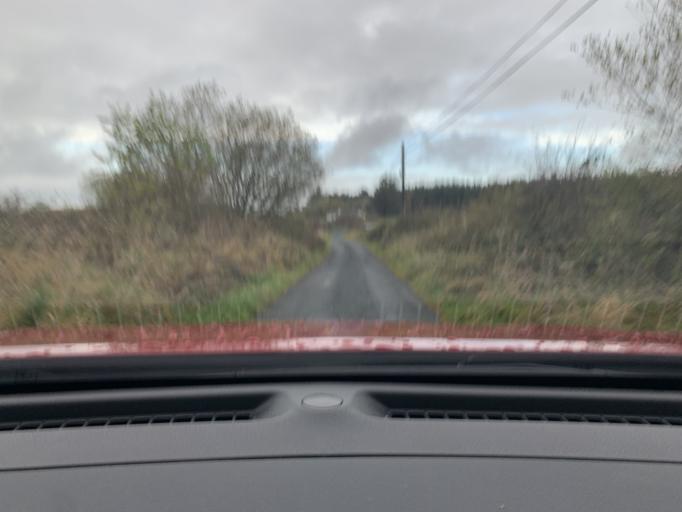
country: IE
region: Connaught
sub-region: Roscommon
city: Ballaghaderreen
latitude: 53.9748
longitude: -8.6084
